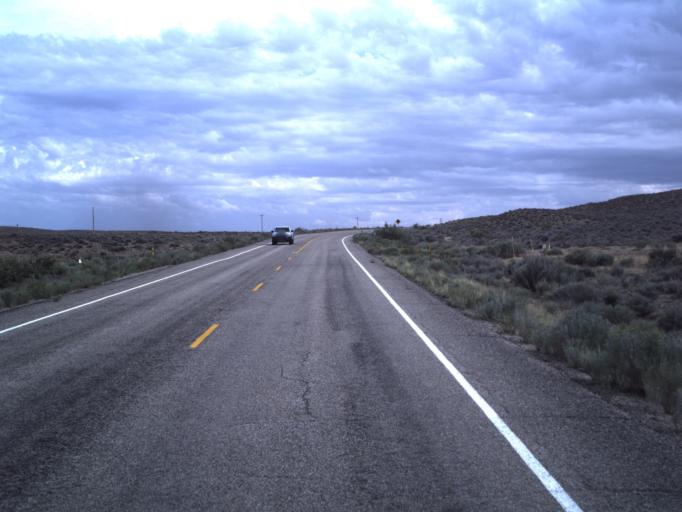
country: US
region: Colorado
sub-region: Rio Blanco County
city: Rangely
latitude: 40.0117
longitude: -109.1697
